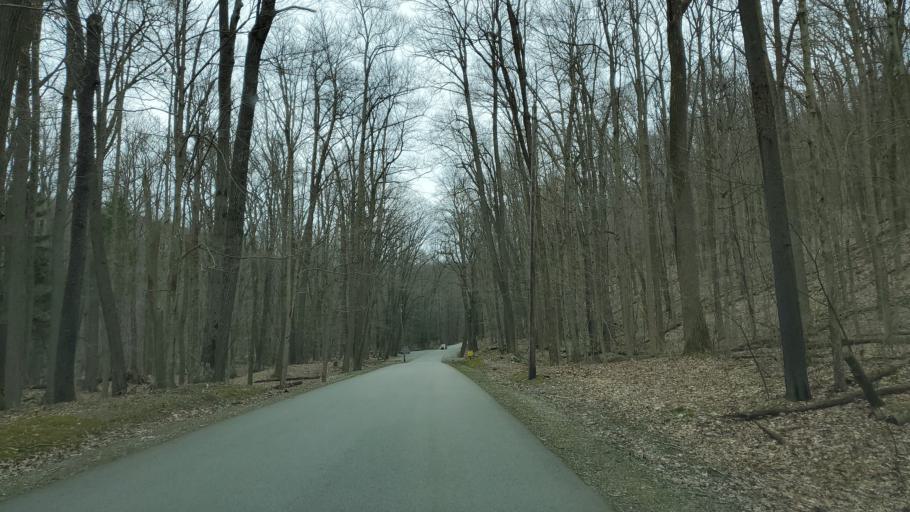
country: US
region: Pennsylvania
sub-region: Westmoreland County
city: Ligonier
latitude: 40.1530
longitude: -79.2247
